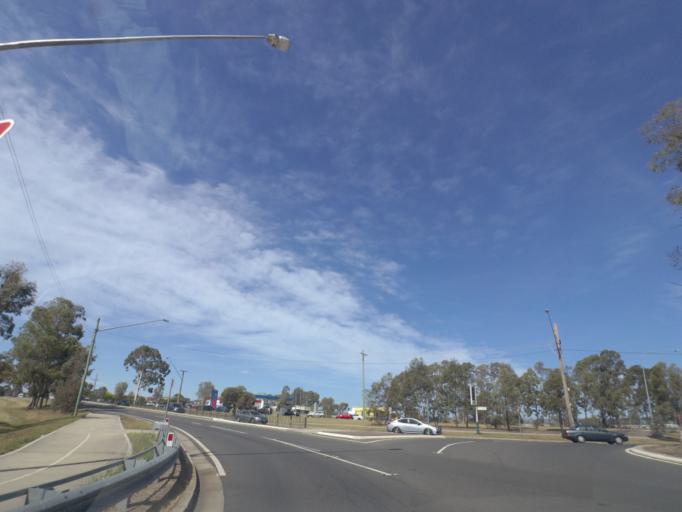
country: AU
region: New South Wales
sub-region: Campbelltown Municipality
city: Leumeah
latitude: -34.0305
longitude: 150.8305
